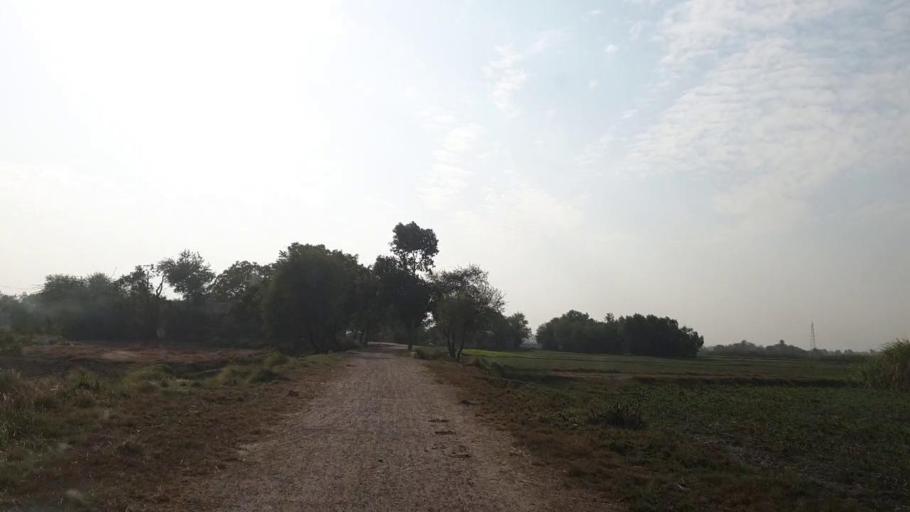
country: PK
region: Sindh
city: Chuhar Jamali
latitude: 24.3854
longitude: 68.0067
